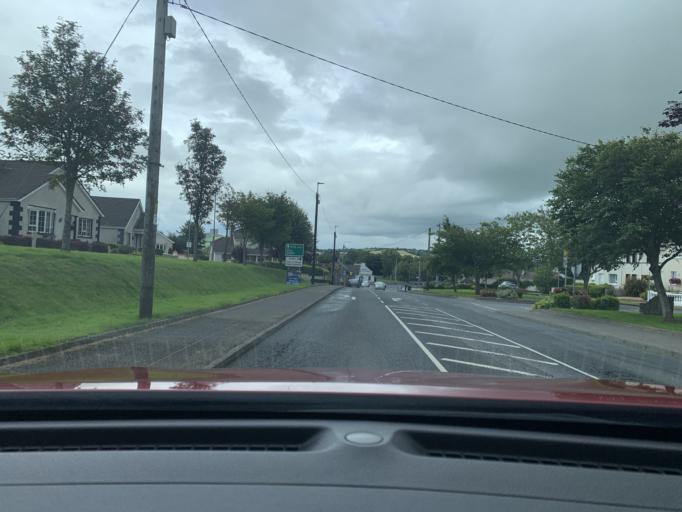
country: IE
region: Ulster
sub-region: County Donegal
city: Raphoe
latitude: 54.8028
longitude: -7.5984
